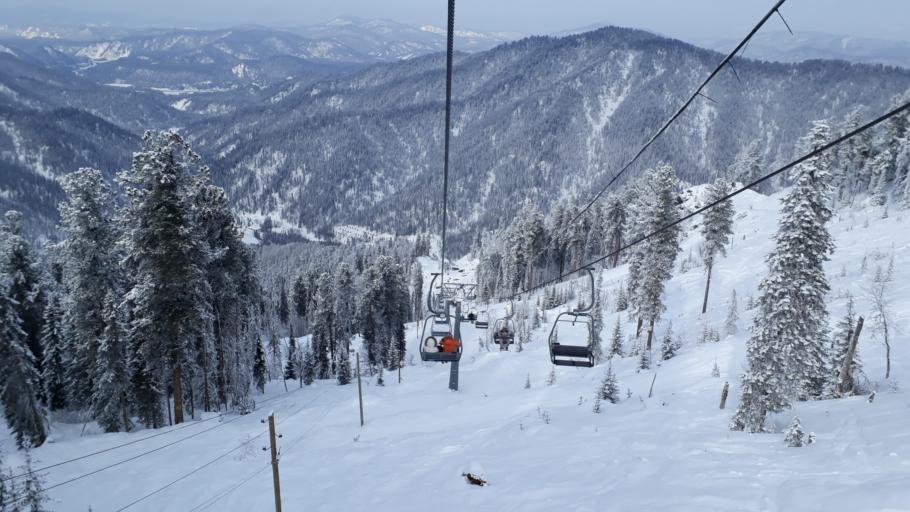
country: RU
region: Altay
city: Iogach
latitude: 51.7317
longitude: 87.2998
